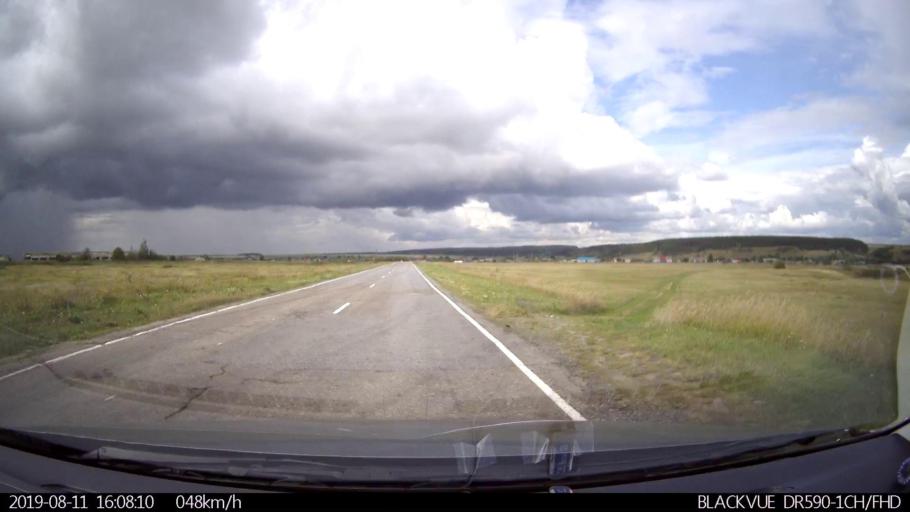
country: RU
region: Ulyanovsk
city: Ignatovka
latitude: 53.9825
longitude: 47.6476
